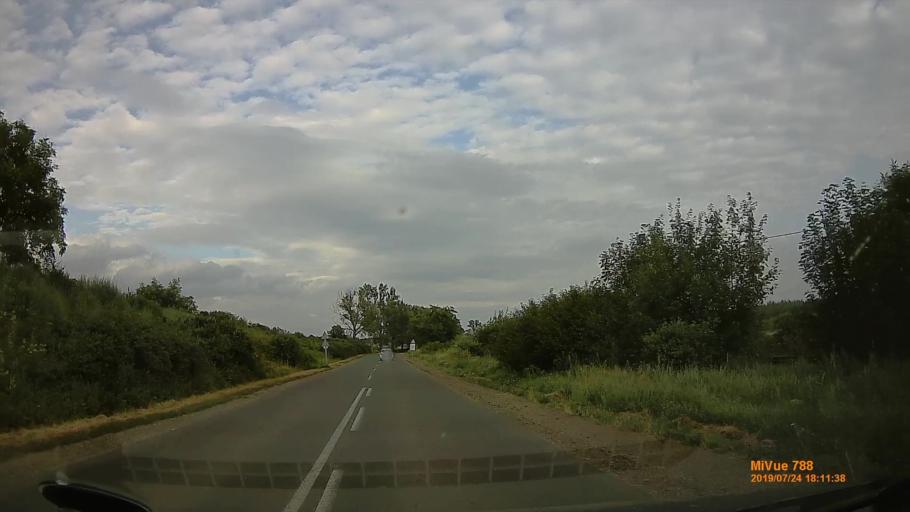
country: HU
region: Borsod-Abauj-Zemplen
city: Tallya
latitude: 48.2444
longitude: 21.2018
